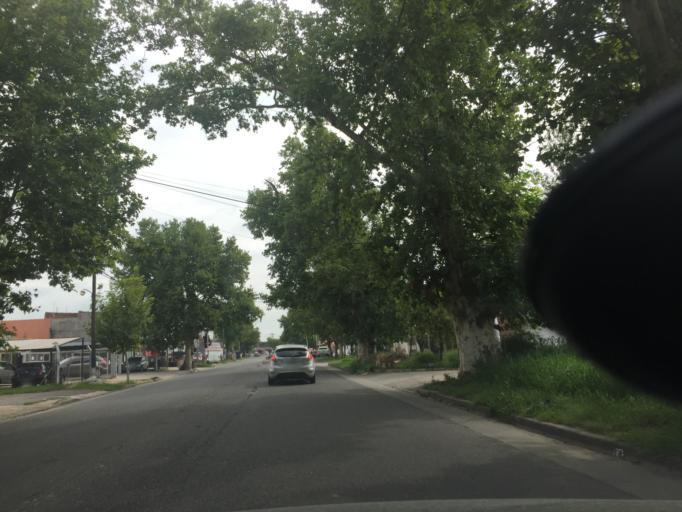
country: AR
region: Cordoba
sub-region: Departamento de Capital
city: Cordoba
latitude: -31.4536
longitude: -64.2062
